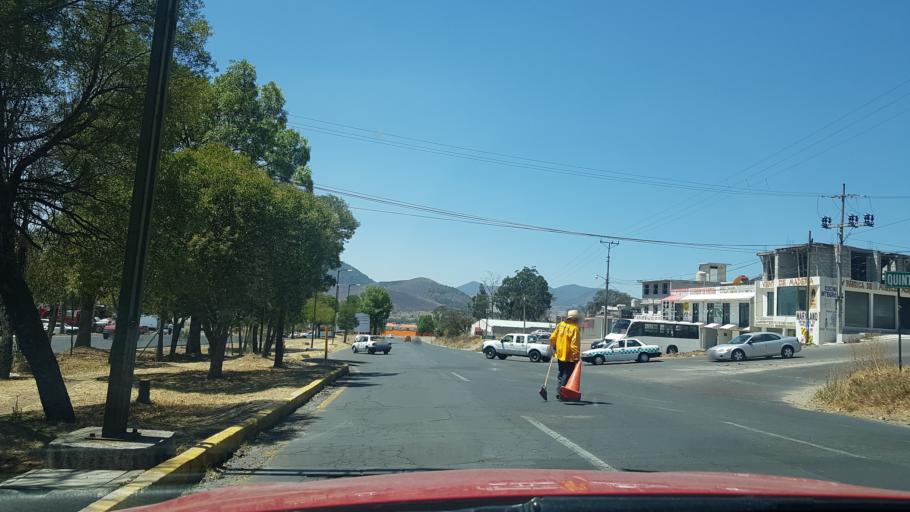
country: MX
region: Mexico
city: Atlacomulco
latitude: 19.8065
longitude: -99.8778
